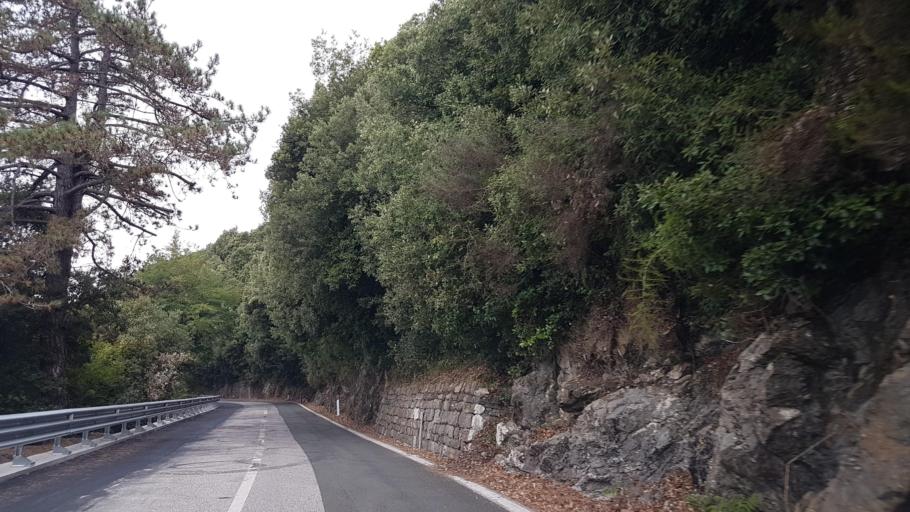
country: IT
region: Liguria
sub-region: Provincia di Genova
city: Castiglione
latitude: 44.2541
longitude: 9.5408
